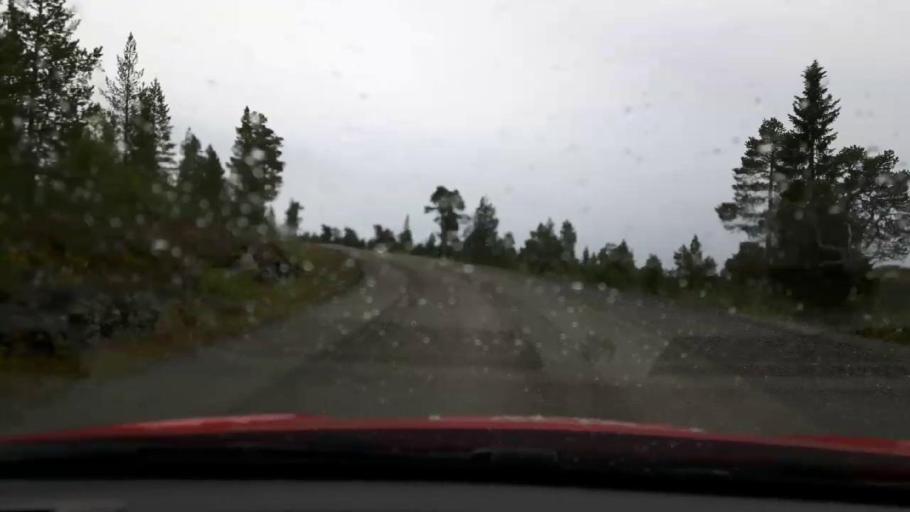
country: NO
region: Nord-Trondelag
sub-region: Meraker
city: Meraker
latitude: 63.6399
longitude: 12.2733
